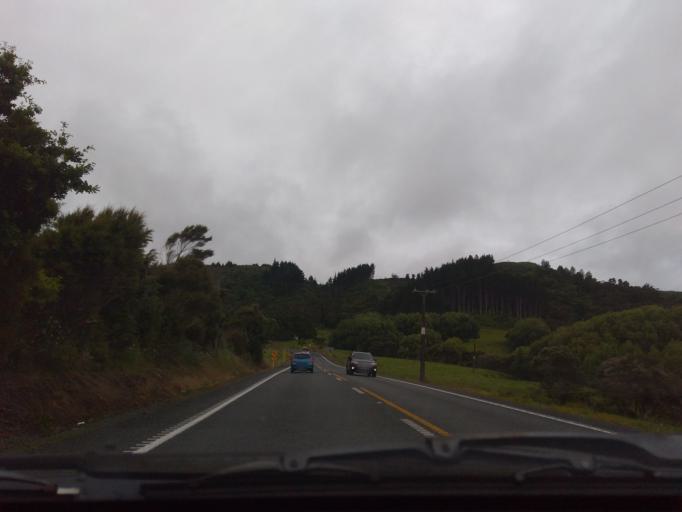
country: NZ
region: Northland
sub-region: Whangarei
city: Ruakaka
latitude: -36.1014
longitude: 174.4332
